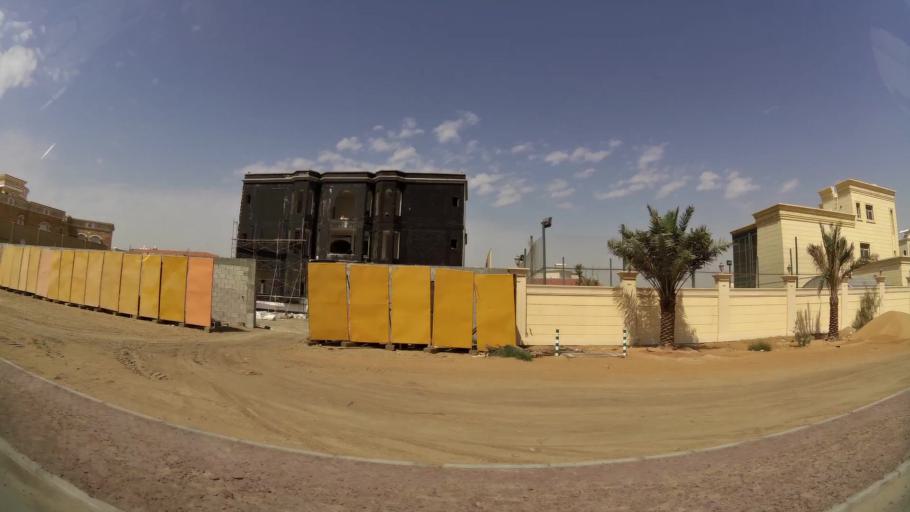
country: AE
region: Abu Dhabi
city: Abu Dhabi
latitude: 24.3156
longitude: 54.5422
